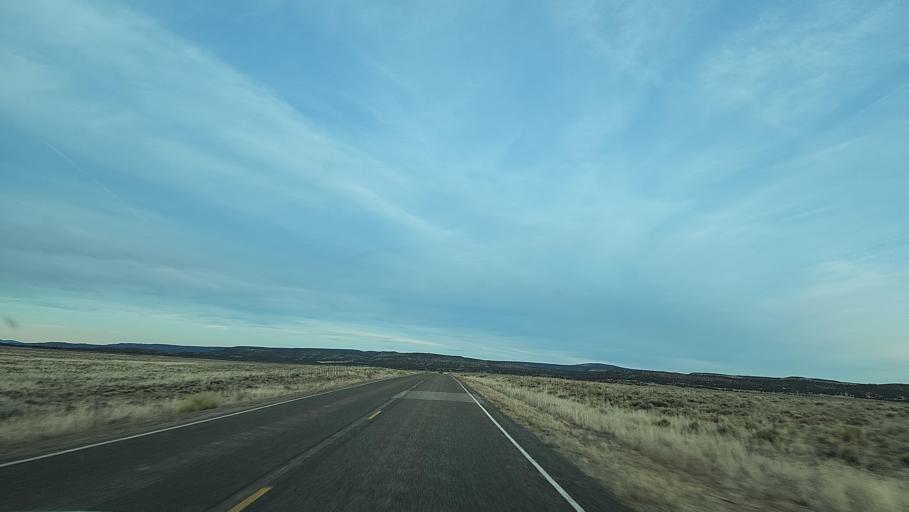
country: US
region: New Mexico
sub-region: Cibola County
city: Grants
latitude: 34.7046
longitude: -108.0219
